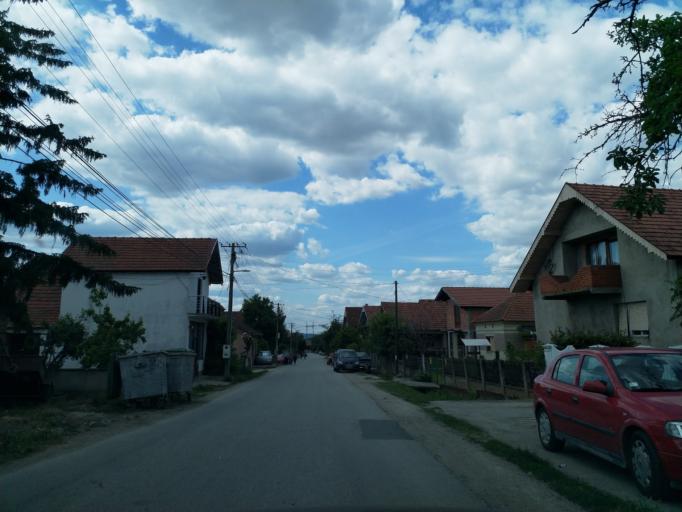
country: RS
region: Central Serbia
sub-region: Pomoravski Okrug
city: Jagodina
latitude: 43.9471
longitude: 21.2957
